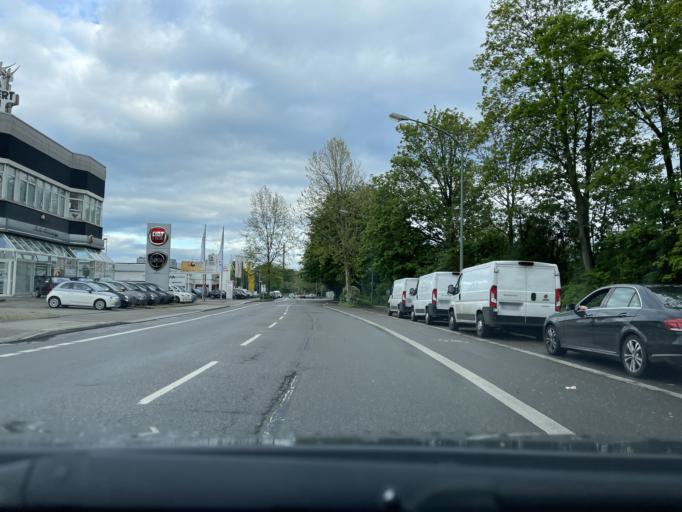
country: DE
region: North Rhine-Westphalia
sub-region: Regierungsbezirk Dusseldorf
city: Essen
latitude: 51.4551
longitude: 6.9844
